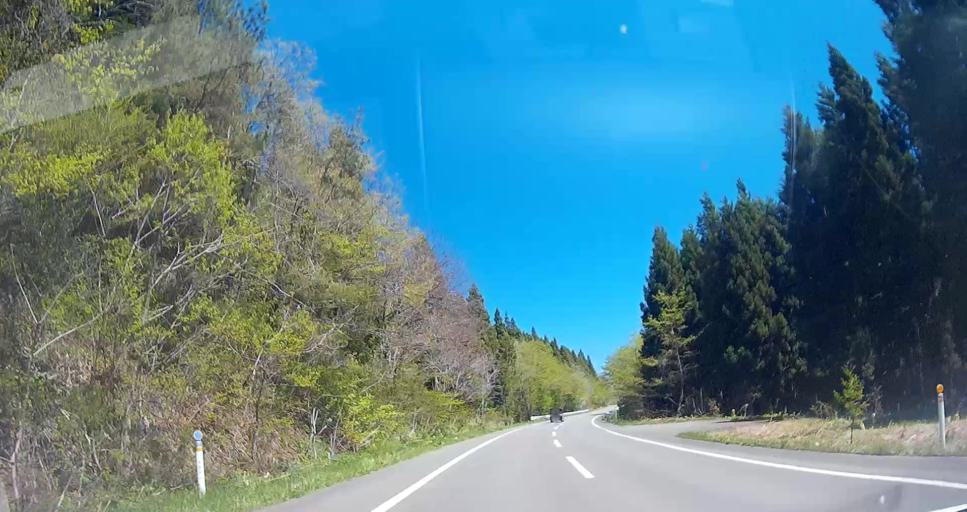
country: JP
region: Aomori
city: Mutsu
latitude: 41.3212
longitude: 141.4060
